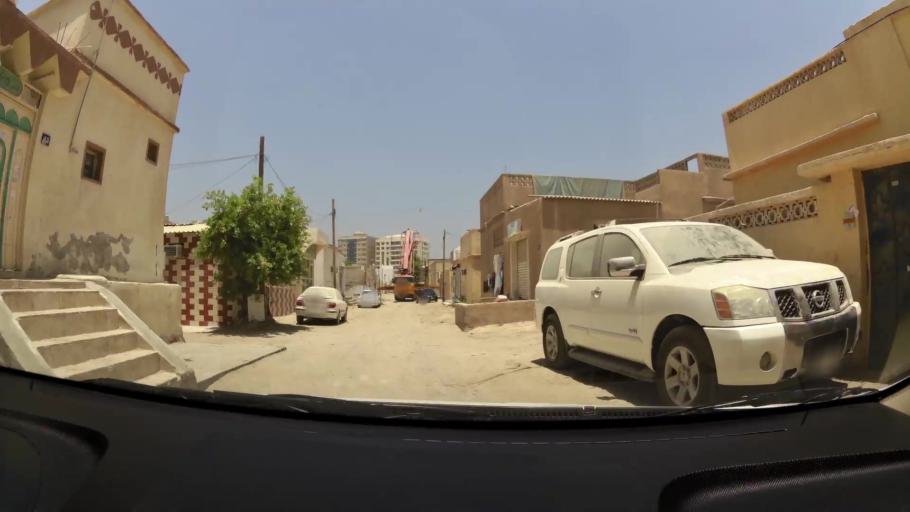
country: AE
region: Ajman
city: Ajman
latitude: 25.3974
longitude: 55.4383
